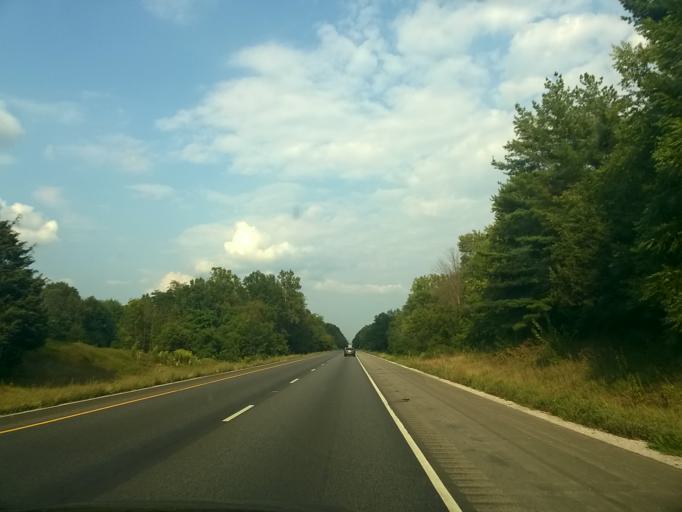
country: US
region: Indiana
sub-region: Clay County
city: Brazil
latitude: 39.4521
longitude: -87.1047
